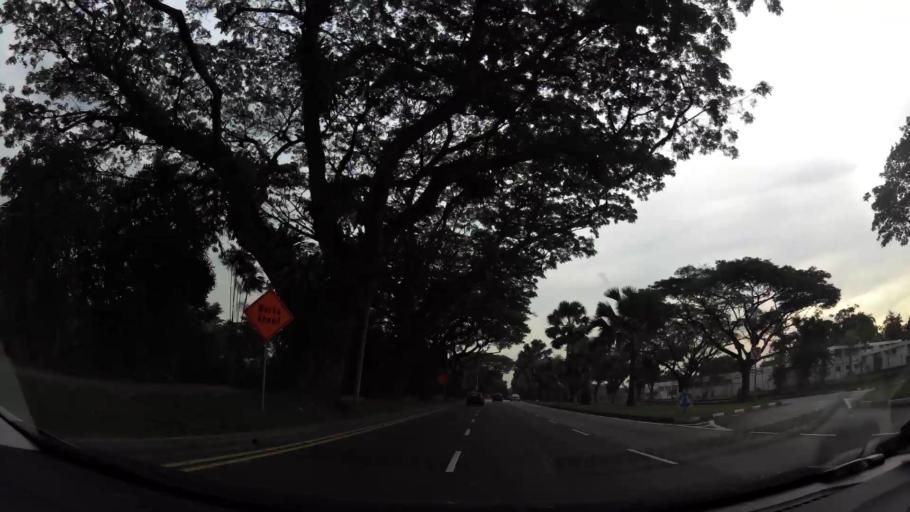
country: MY
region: Johor
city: Kampung Pasir Gudang Baru
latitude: 1.4213
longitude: 103.8251
